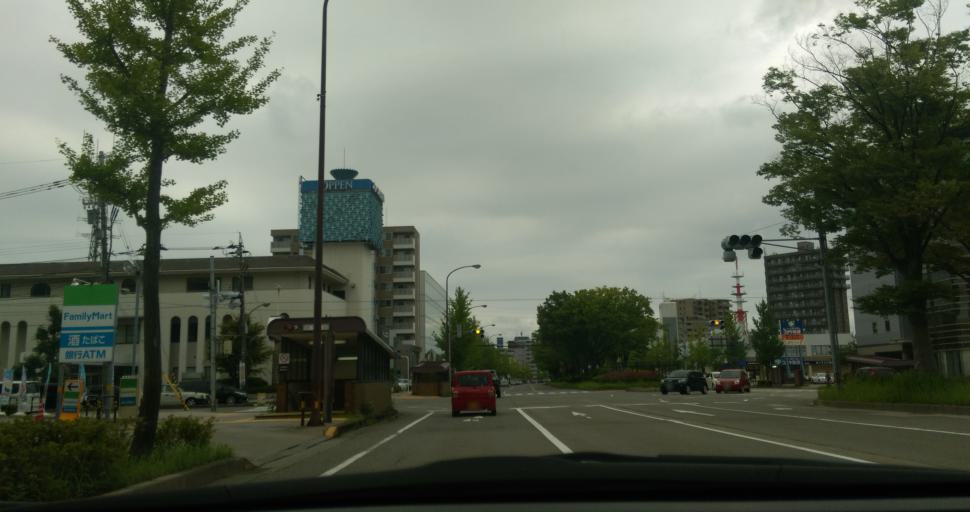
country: JP
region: Ishikawa
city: Kanazawa-shi
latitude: 36.5823
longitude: 136.6408
